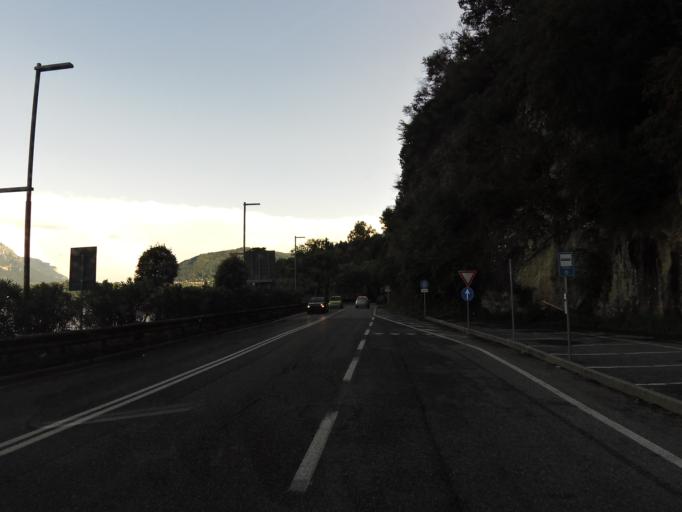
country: IT
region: Lombardy
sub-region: Provincia di Como
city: Griante
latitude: 46.0043
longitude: 9.2344
